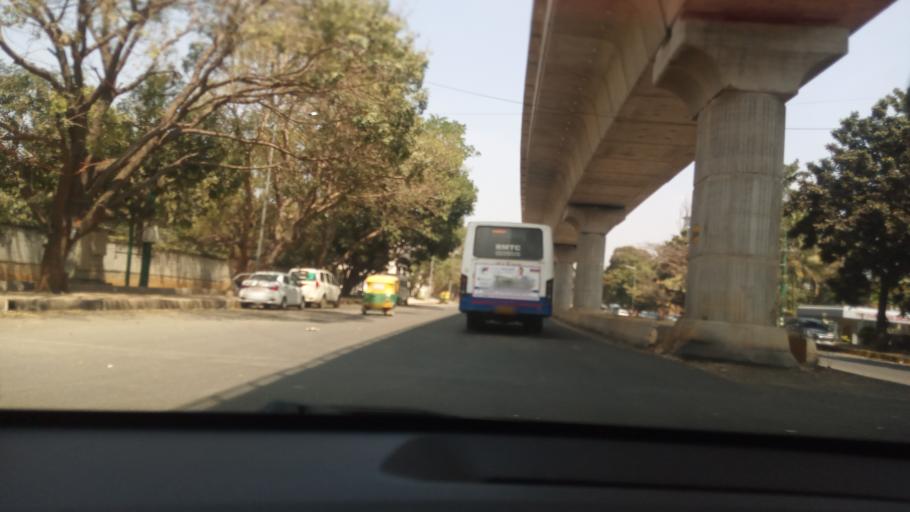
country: IN
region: Karnataka
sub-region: Bangalore Rural
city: Hoskote
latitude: 12.9843
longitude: 77.7290
